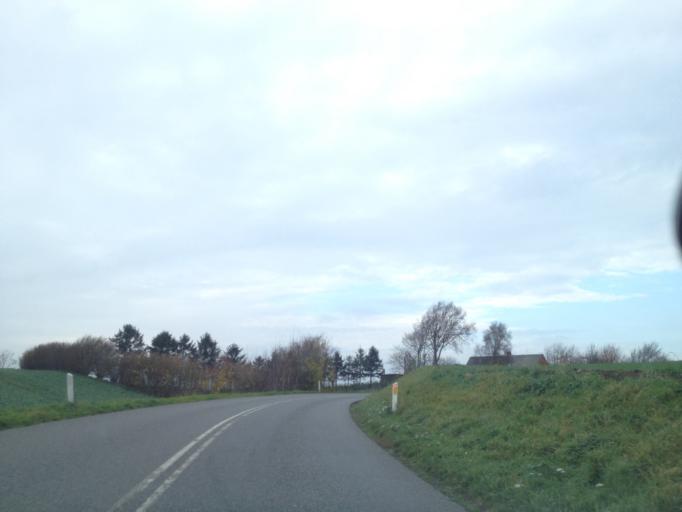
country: DK
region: South Denmark
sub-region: Assens Kommune
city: Vissenbjerg
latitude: 55.4045
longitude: 10.1575
